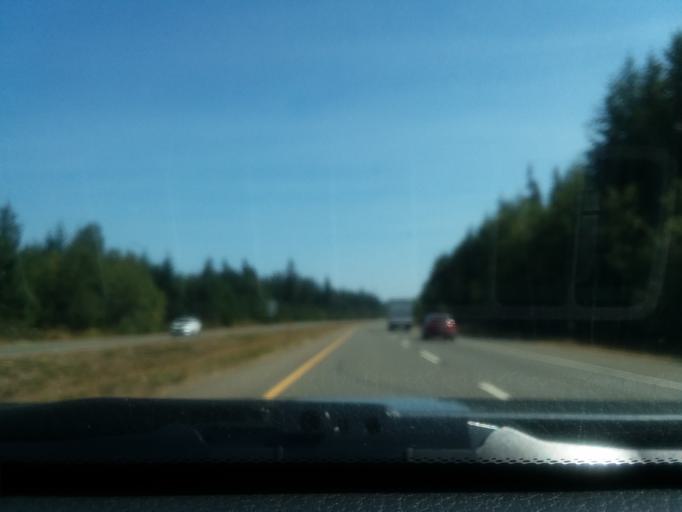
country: CA
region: British Columbia
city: Port Alberni
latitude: 49.3968
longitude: -124.6547
